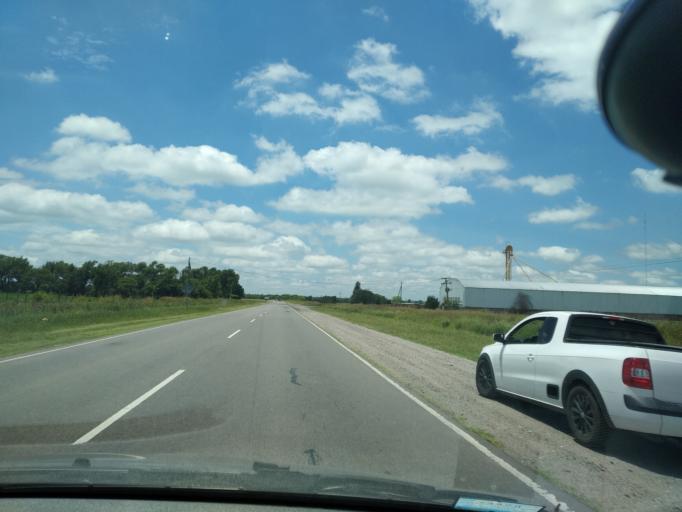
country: AR
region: Cordoba
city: Alta Gracia
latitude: -31.6581
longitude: -64.3629
